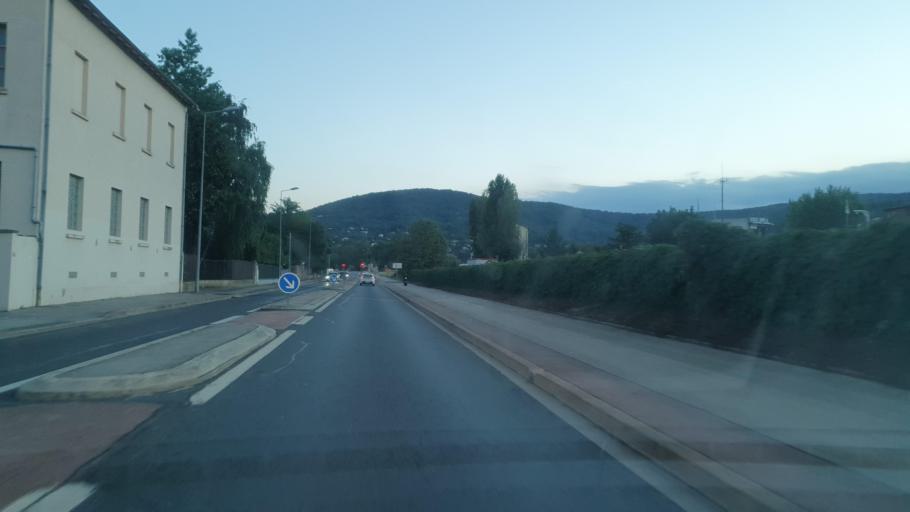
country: FR
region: Rhone-Alpes
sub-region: Departement du Rhone
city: Rochetaillee-sur-Saone
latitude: 45.8478
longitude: 4.8364
